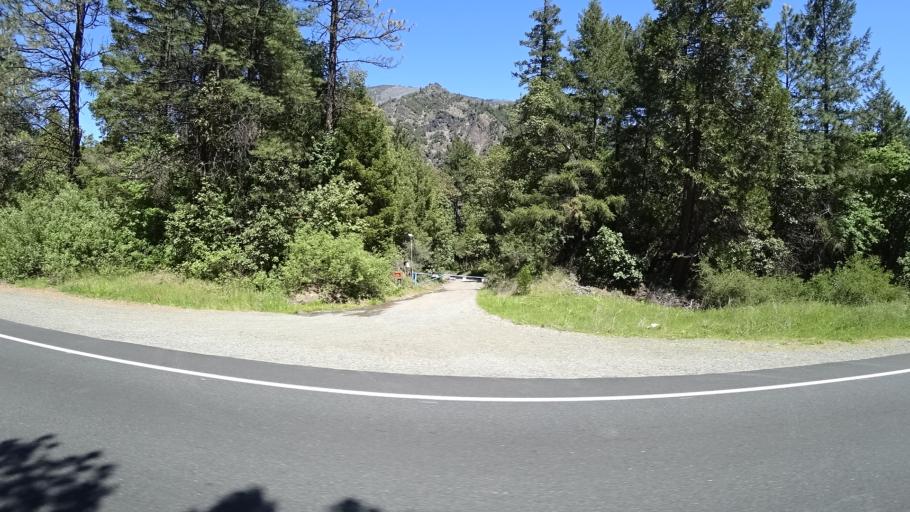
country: US
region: California
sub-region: Humboldt County
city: Willow Creek
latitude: 40.8079
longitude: -123.4736
